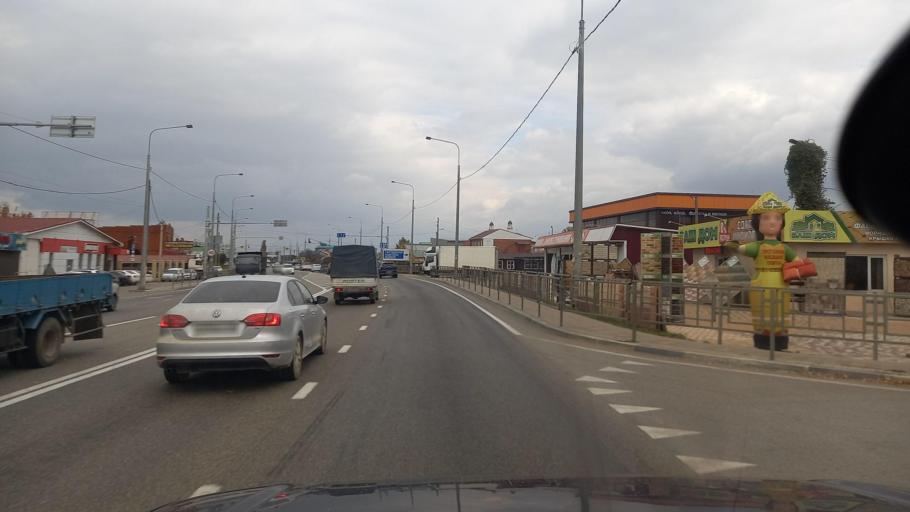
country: RU
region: Adygeya
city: Enem
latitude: 44.9288
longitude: 38.9092
